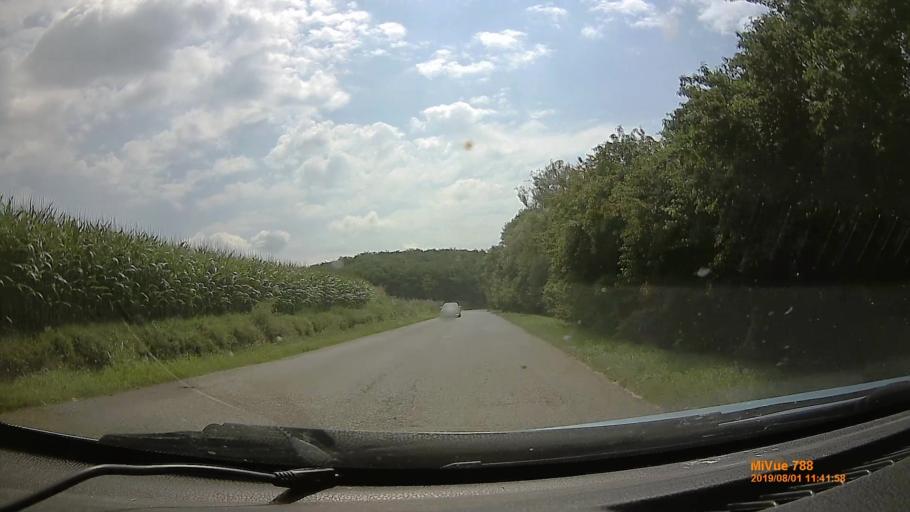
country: HU
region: Baranya
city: Villany
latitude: 45.8891
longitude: 18.4101
